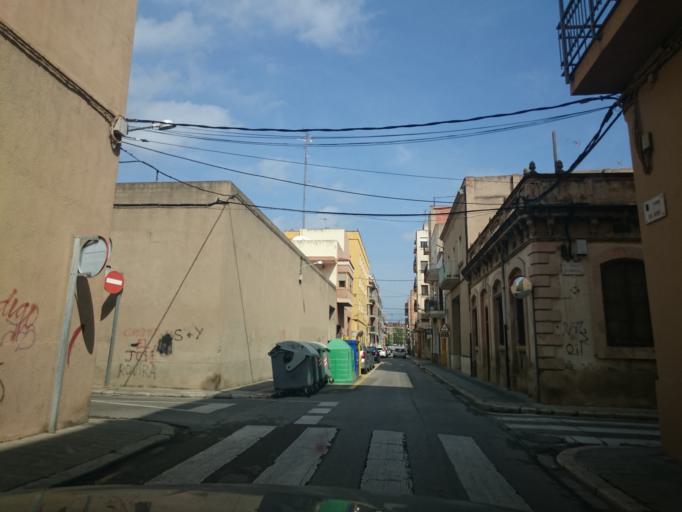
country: ES
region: Catalonia
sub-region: Provincia de Girona
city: Figueres
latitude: 42.2678
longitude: 2.9682
